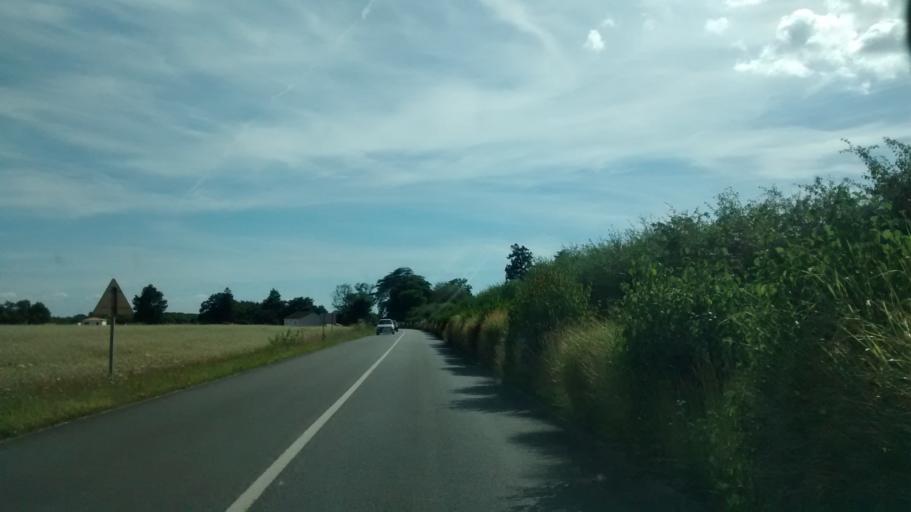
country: FR
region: Pays de la Loire
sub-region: Departement de la Loire-Atlantique
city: Pont-Saint-Martin
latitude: 47.1439
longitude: -1.6050
